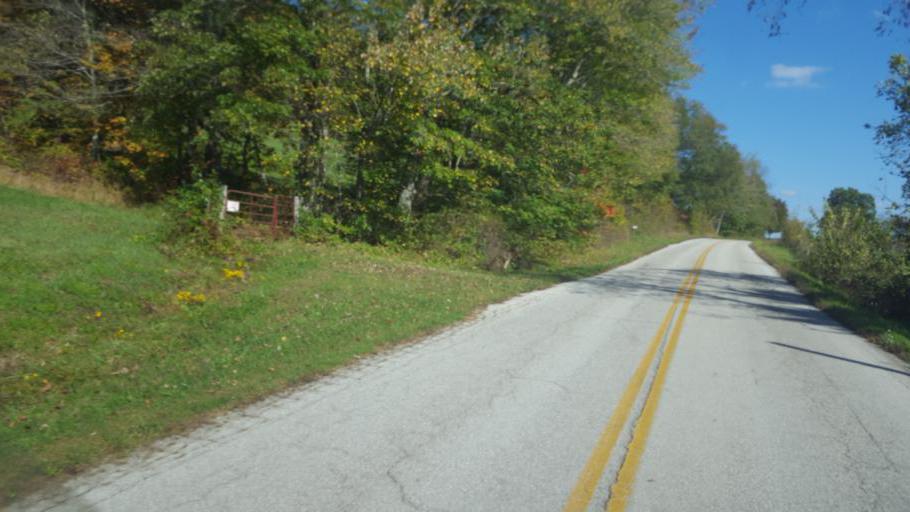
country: US
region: Kentucky
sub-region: Fleming County
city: Flemingsburg
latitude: 38.4687
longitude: -83.5589
